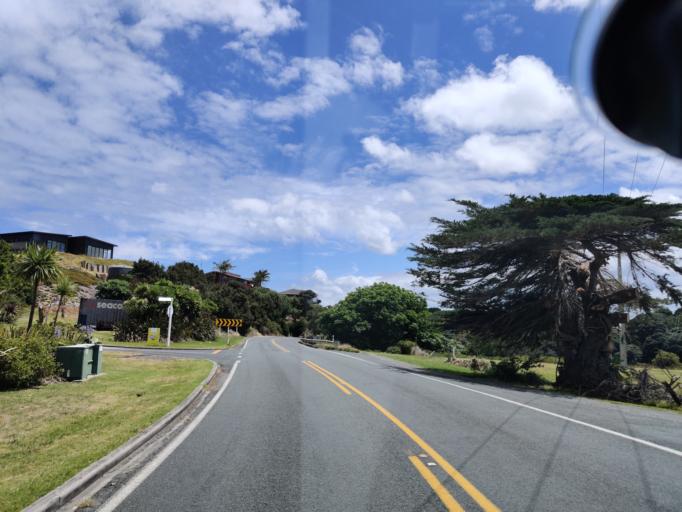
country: NZ
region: Northland
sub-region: Far North District
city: Kaitaia
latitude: -34.8132
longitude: 173.1175
